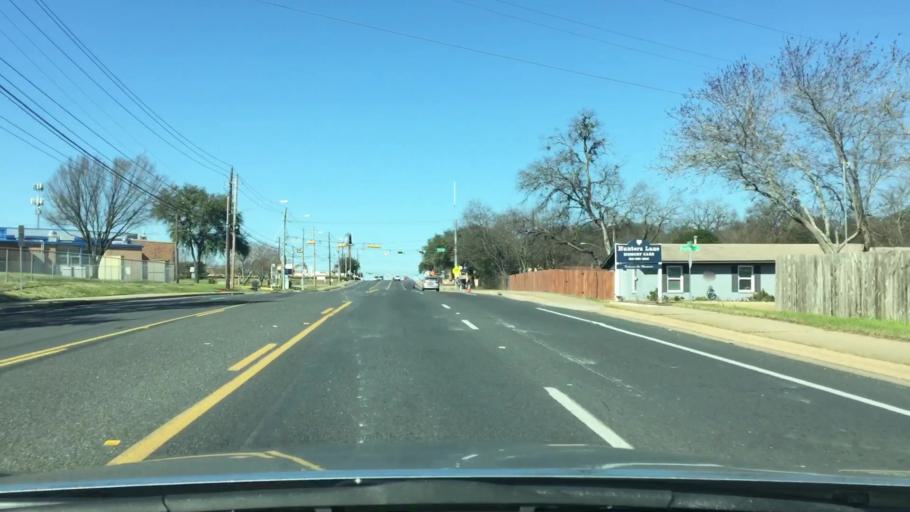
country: US
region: Texas
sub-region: Travis County
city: Wells Branch
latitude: 30.3796
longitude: -97.6824
